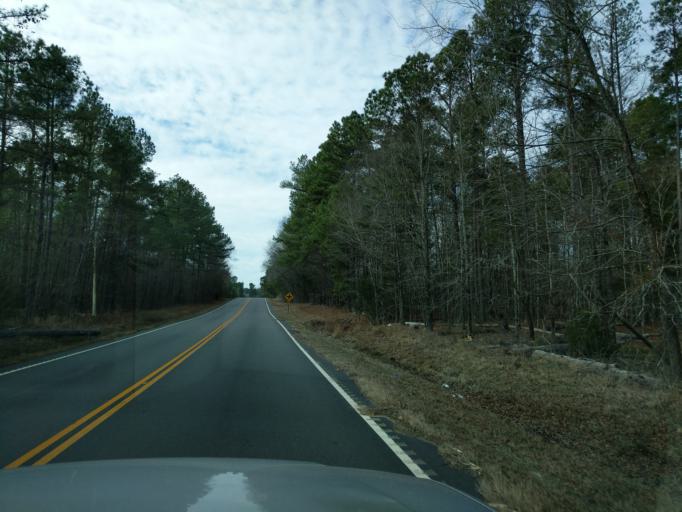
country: US
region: South Carolina
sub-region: Edgefield County
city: Edgefield
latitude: 33.9299
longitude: -81.9951
